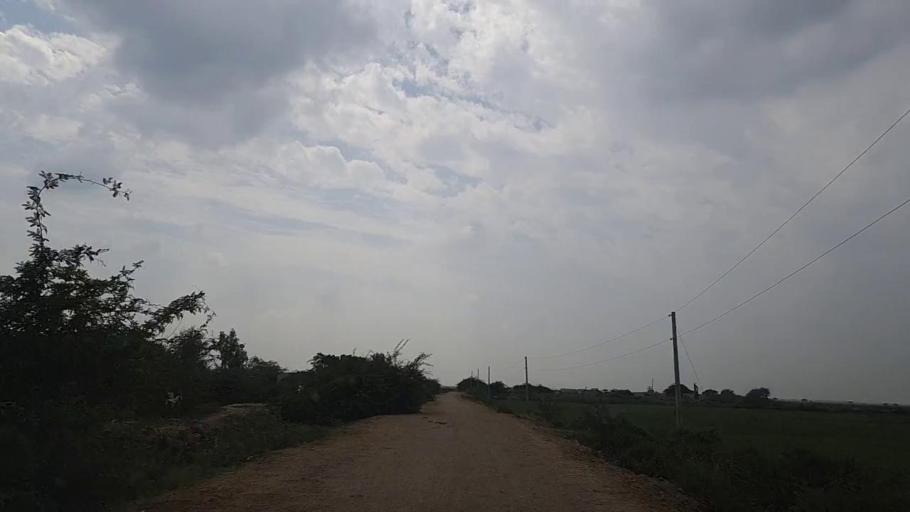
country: PK
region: Sindh
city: Mirpur Batoro
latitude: 24.6219
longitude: 68.1372
